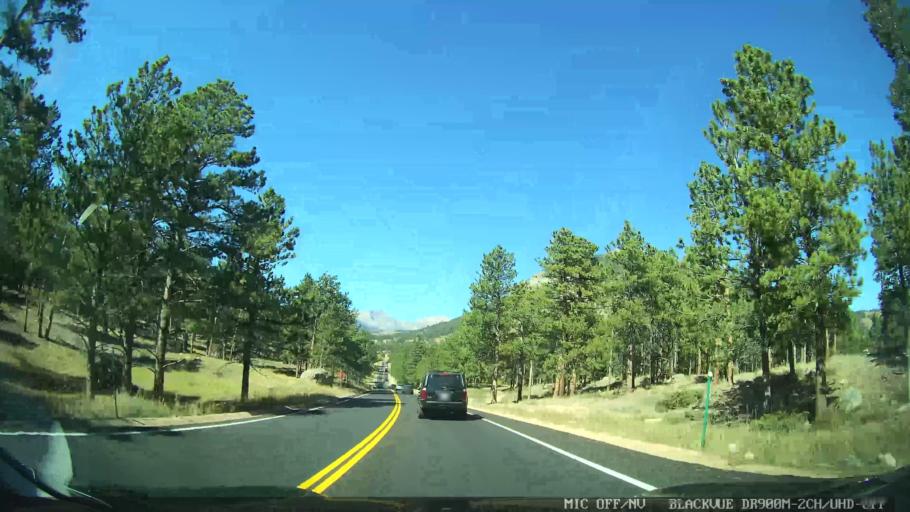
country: US
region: Colorado
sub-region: Larimer County
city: Estes Park
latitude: 40.3615
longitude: -105.5817
